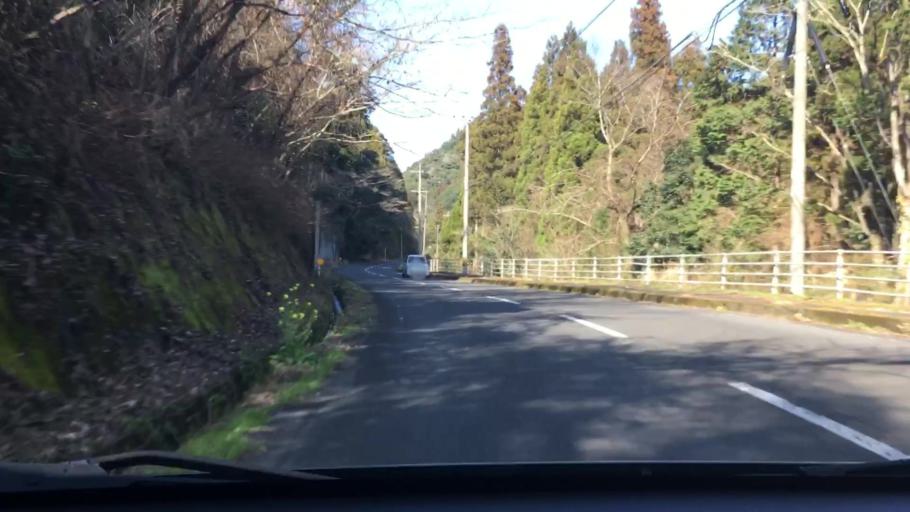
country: JP
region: Kagoshima
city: Satsumasendai
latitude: 31.7503
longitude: 130.4111
